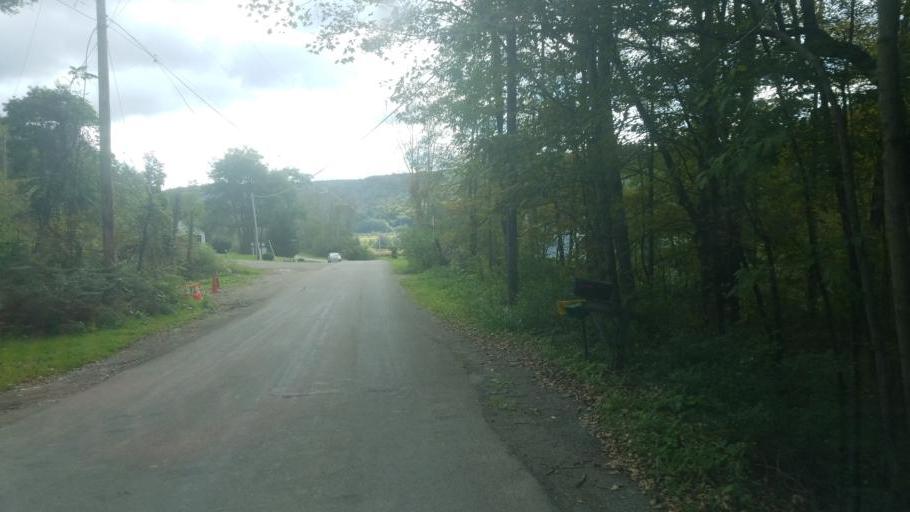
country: US
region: New York
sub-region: Allegany County
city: Cuba
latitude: 42.2185
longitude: -78.3300
